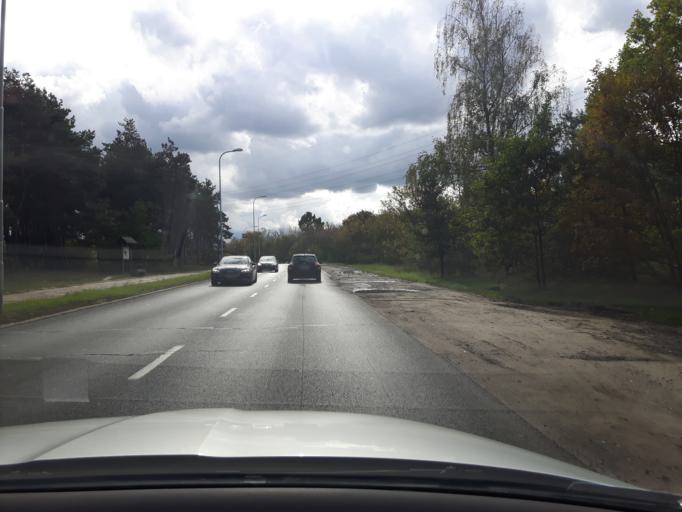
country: PL
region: Masovian Voivodeship
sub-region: Warszawa
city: Rembertow
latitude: 52.2314
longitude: 21.1437
